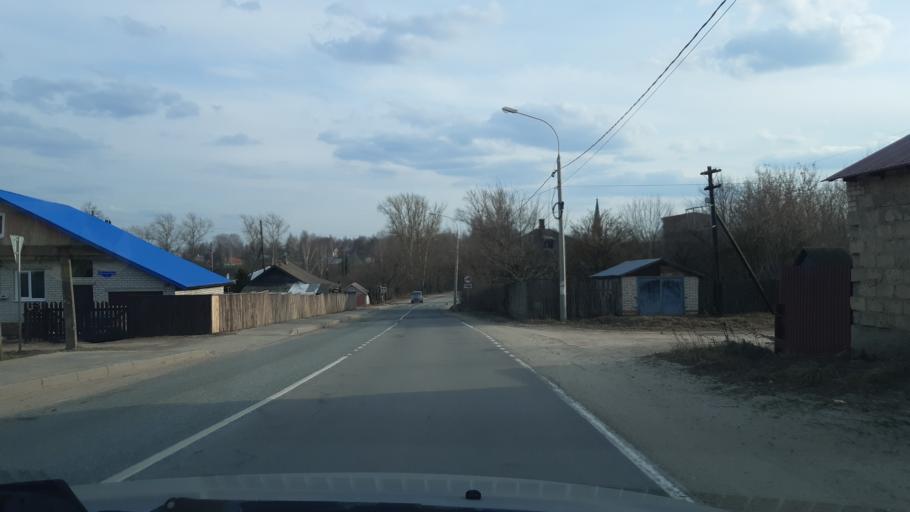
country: RU
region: Vladimir
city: Nikologory
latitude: 56.1451
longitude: 41.9933
